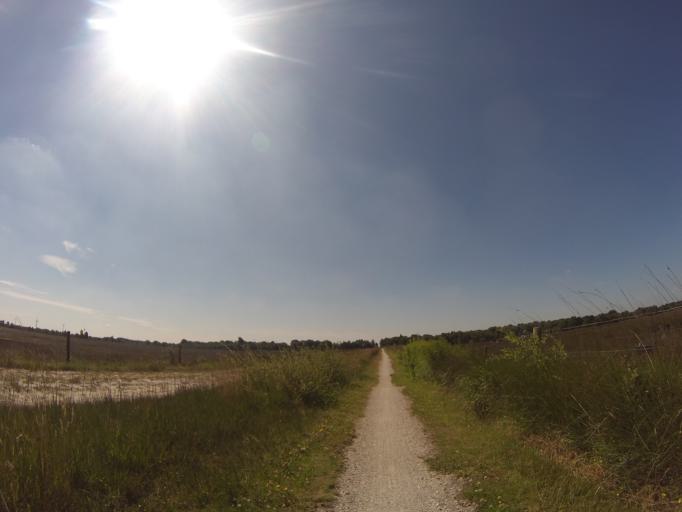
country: DE
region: Lower Saxony
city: Twist
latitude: 52.6745
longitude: 7.0231
